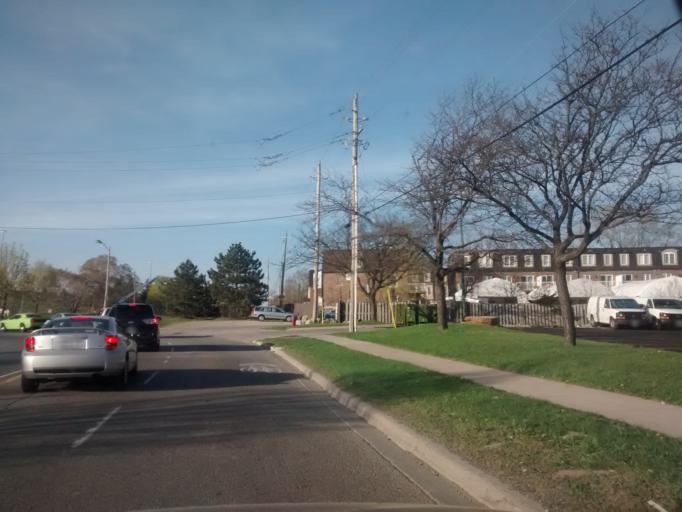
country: CA
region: Ontario
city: Burlington
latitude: 43.3437
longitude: -79.8122
